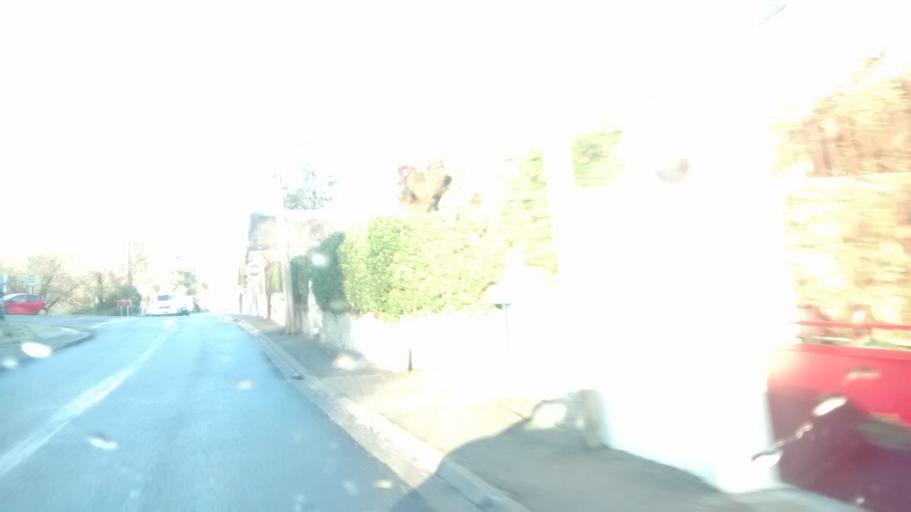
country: FR
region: Centre
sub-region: Departement d'Indre-et-Loire
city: Esvres
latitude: 47.2819
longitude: 0.7903
